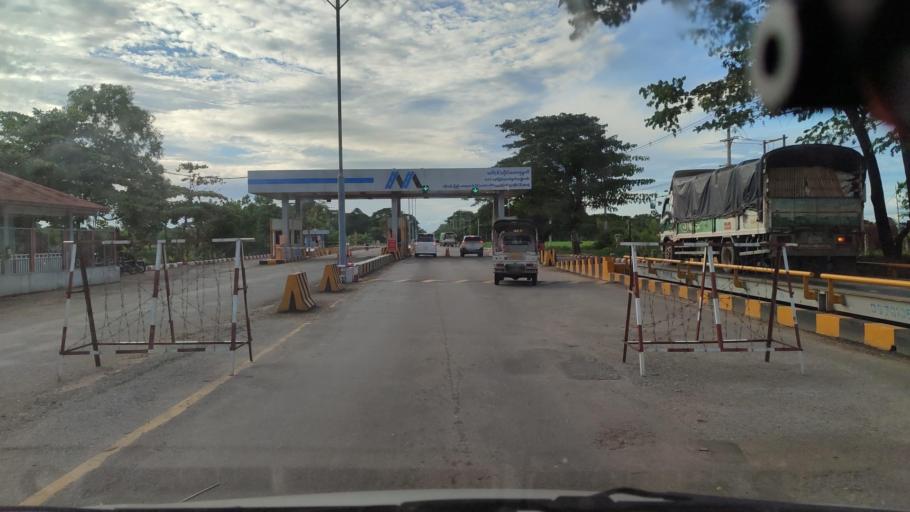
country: MM
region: Bago
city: Tharyarwady
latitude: 17.6988
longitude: 95.7818
